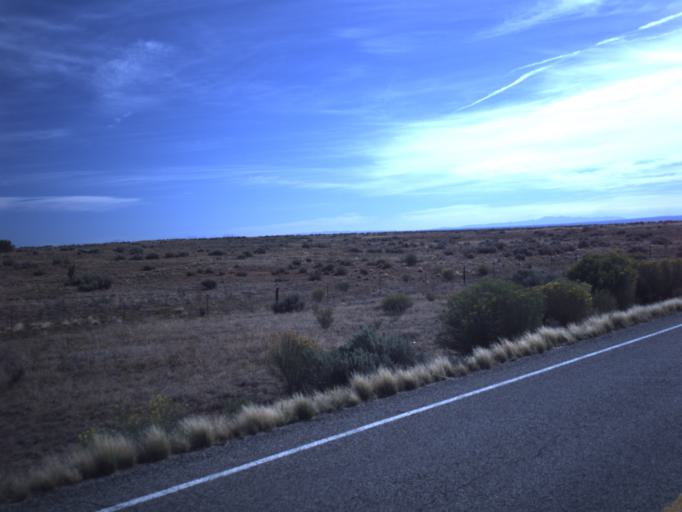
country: US
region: Utah
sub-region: San Juan County
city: Blanding
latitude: 37.4323
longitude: -109.3679
